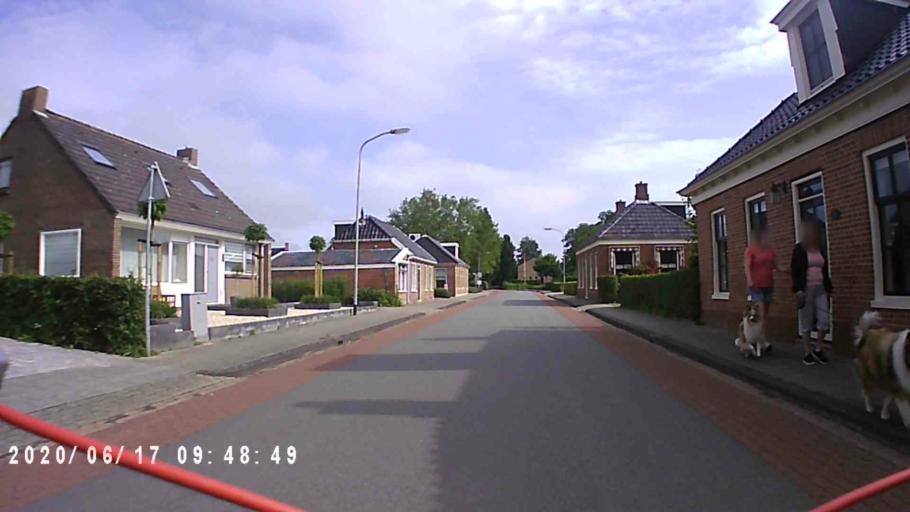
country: NL
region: Groningen
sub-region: Gemeente De Marne
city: Ulrum
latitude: 53.3586
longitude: 6.3384
